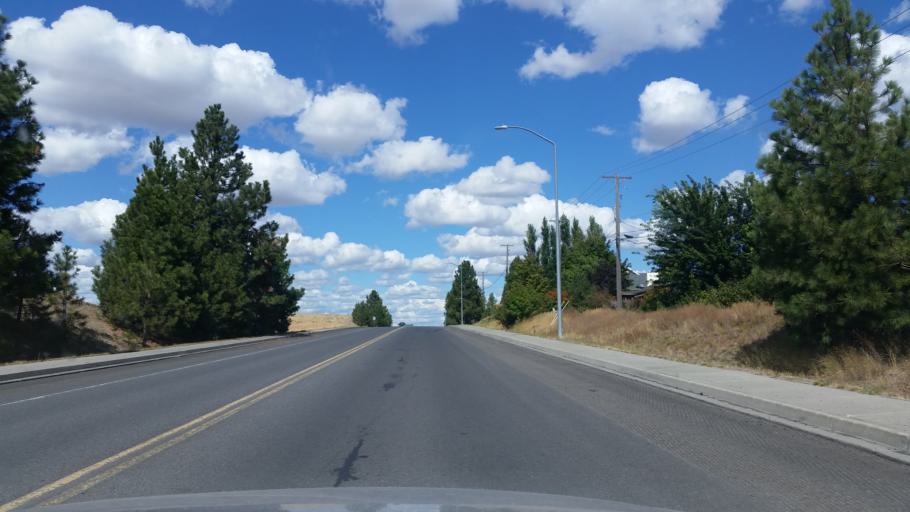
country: US
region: Washington
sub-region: Spokane County
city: Cheney
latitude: 47.4977
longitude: -117.5865
